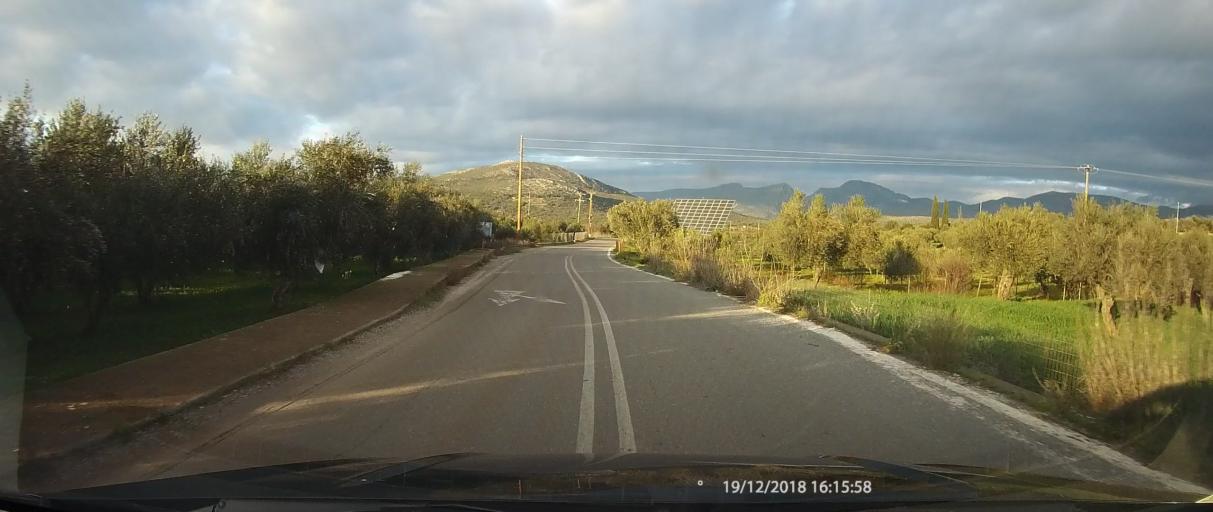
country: GR
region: Peloponnese
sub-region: Nomos Lakonias
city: Kato Glikovrisi
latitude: 36.8943
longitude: 22.8026
